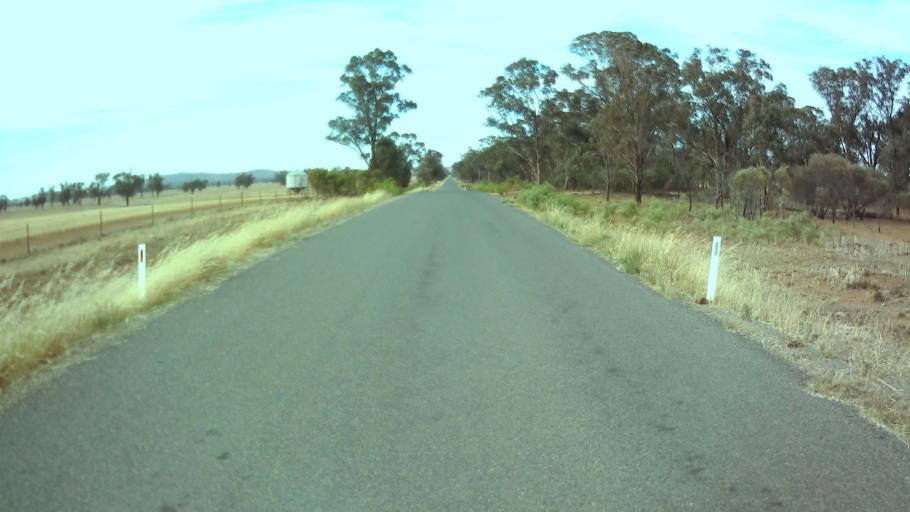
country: AU
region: New South Wales
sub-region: Weddin
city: Grenfell
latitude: -33.8853
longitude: 147.8553
